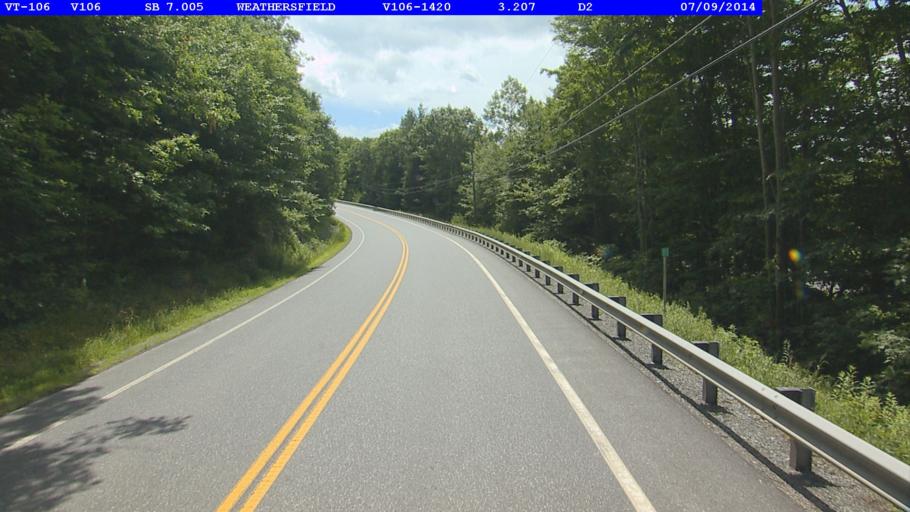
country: US
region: Vermont
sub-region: Windsor County
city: Springfield
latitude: 43.3847
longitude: -72.5126
